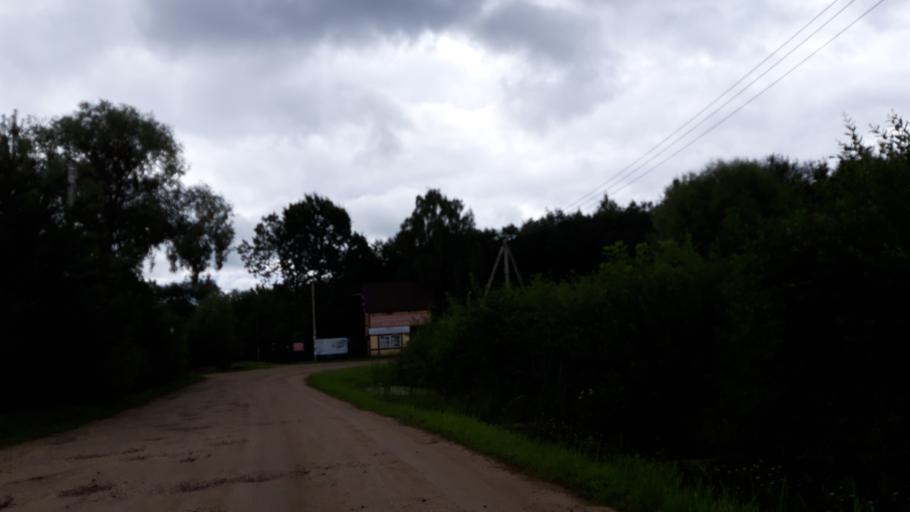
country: RU
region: Tverskaya
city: Konakovo
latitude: 56.6814
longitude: 36.7128
